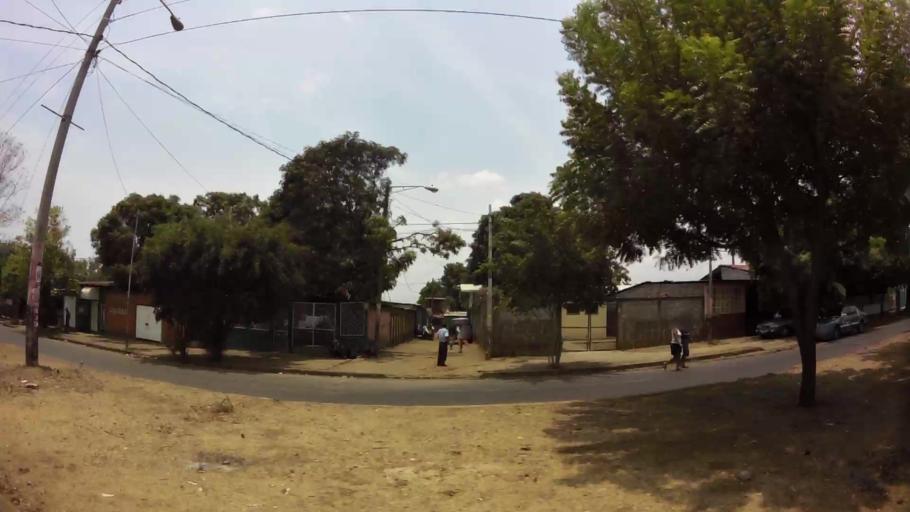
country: NI
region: Managua
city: Managua
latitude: 12.1320
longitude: -86.2904
